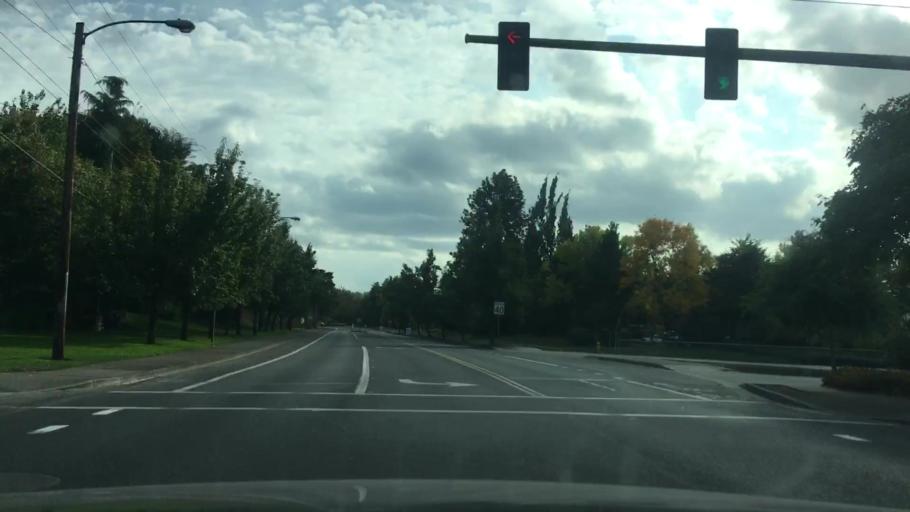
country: US
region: Oregon
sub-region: Lane County
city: Eugene
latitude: 44.0840
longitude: -123.1113
